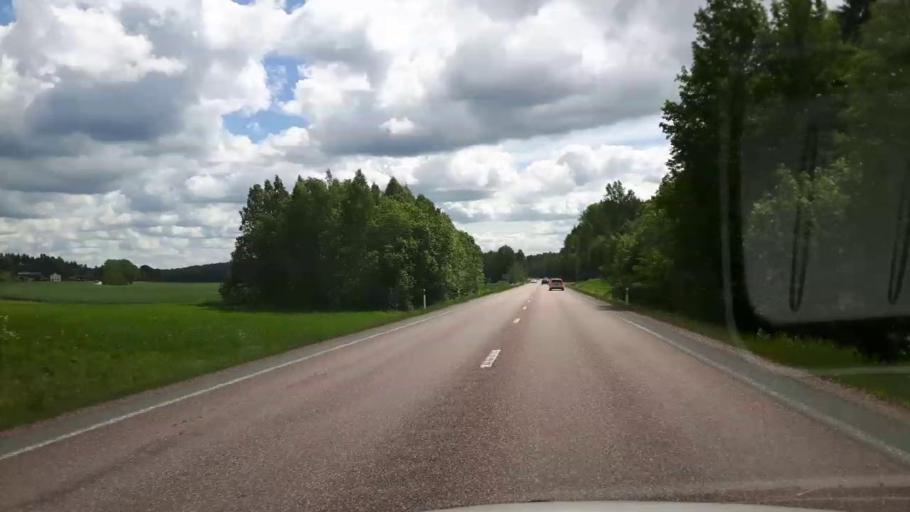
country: SE
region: Dalarna
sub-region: Saters Kommun
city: Saeter
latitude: 60.4806
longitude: 15.7761
